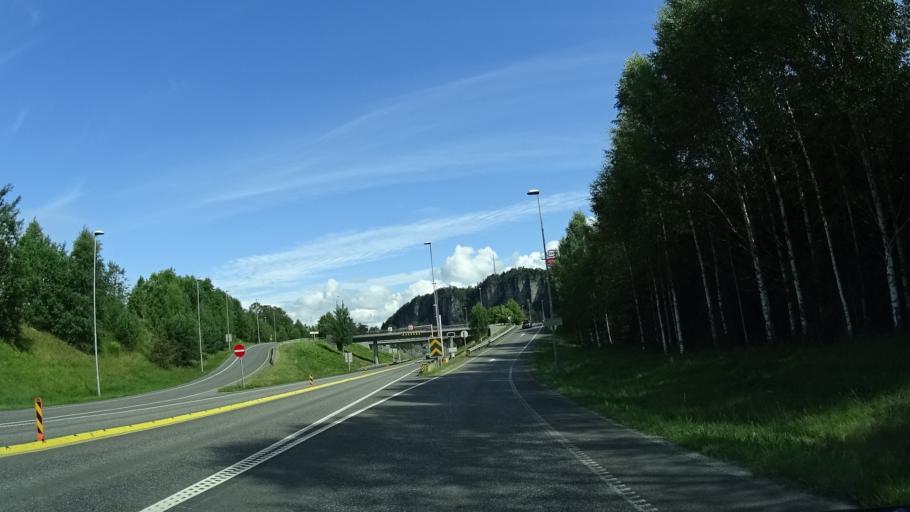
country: NO
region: Telemark
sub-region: Bamble
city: Langesund
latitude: 59.0343
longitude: 9.6770
